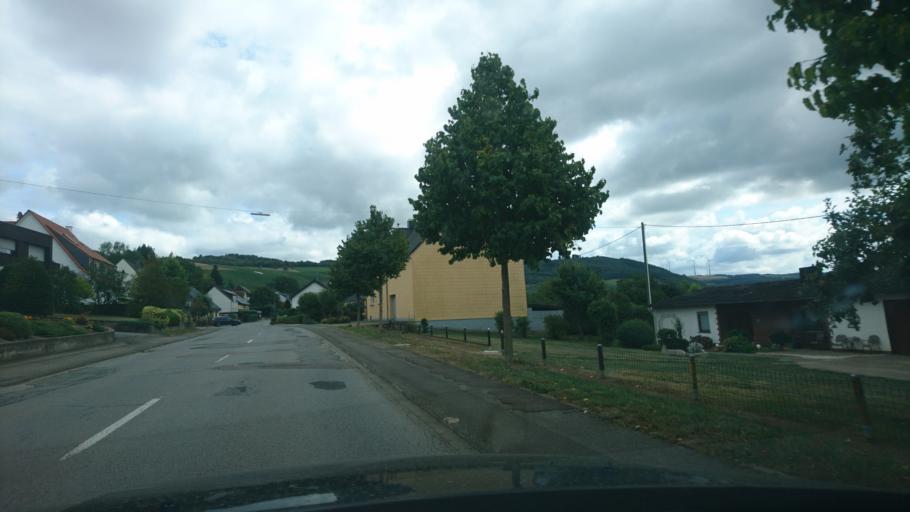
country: DE
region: Rheinland-Pfalz
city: Wiltingen
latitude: 49.6930
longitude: 6.6316
